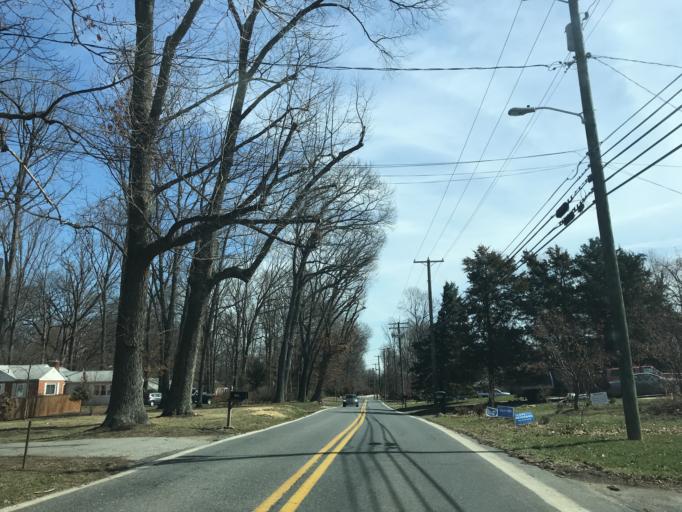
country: US
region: Maryland
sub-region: Montgomery County
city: Ashton-Sandy Spring
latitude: 39.1387
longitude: -76.9876
